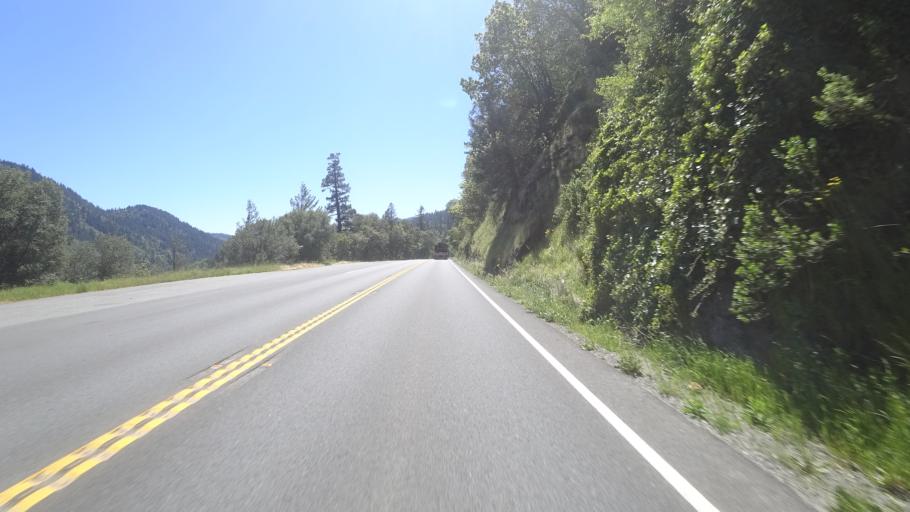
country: US
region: California
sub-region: Humboldt County
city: Willow Creek
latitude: 40.9148
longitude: -123.6168
